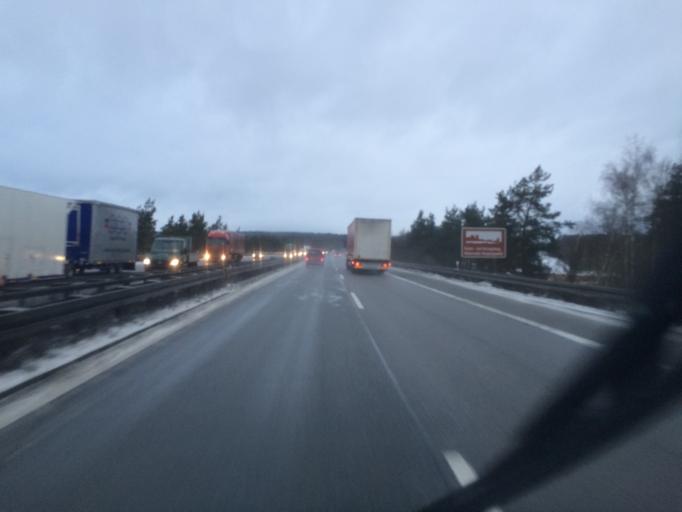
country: DE
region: Bavaria
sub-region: Upper Palatinate
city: Regenstauf
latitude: 49.1370
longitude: 12.1071
